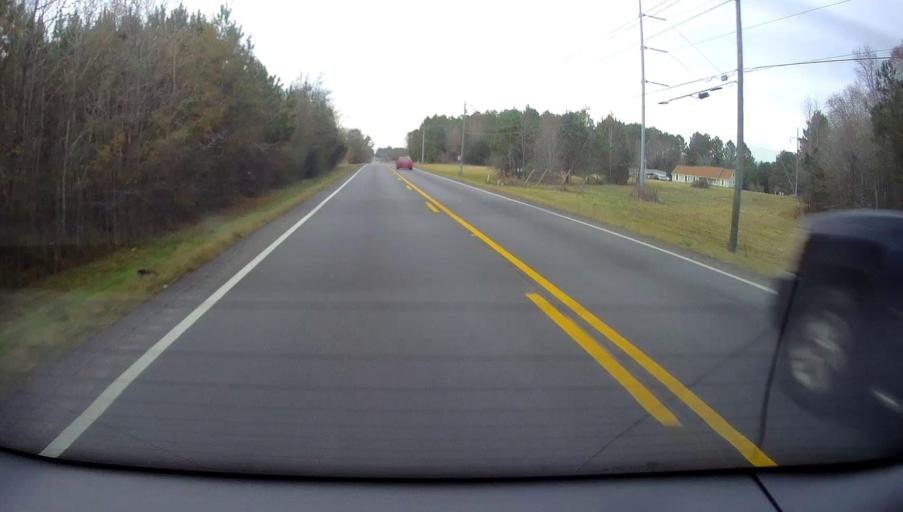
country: US
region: Alabama
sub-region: Morgan County
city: Priceville
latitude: 34.4508
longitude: -86.7636
